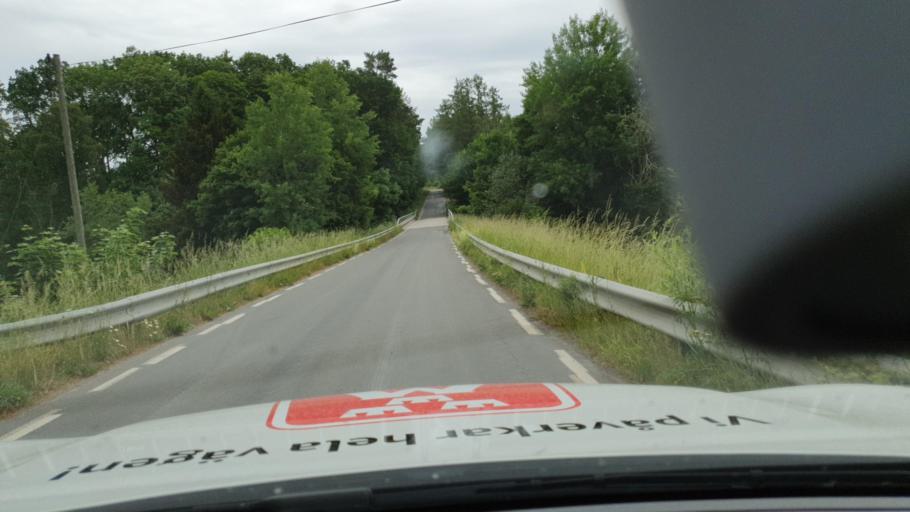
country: SE
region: Vaestra Goetaland
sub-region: Tidaholms Kommun
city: Olofstorp
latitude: 58.3217
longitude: 14.0976
